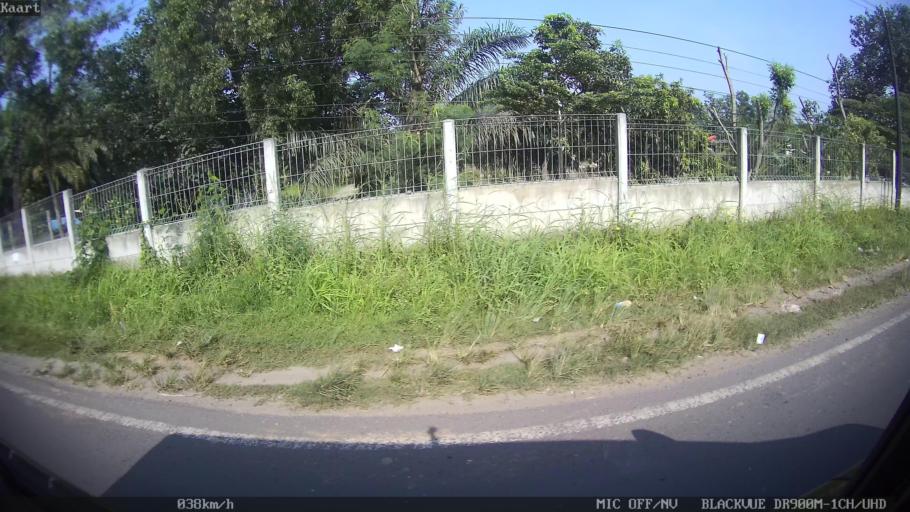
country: ID
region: Lampung
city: Natar
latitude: -5.2352
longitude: 105.1727
